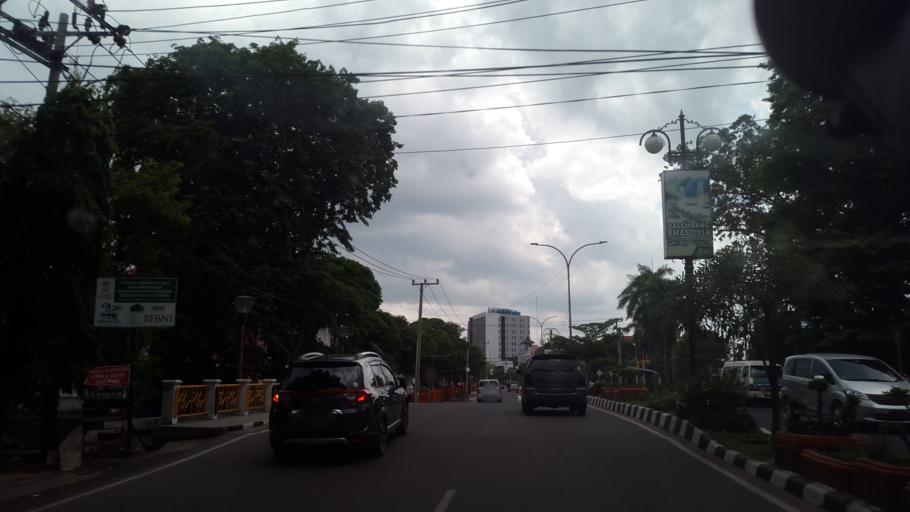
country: ID
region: South Sumatra
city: Plaju
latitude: -2.9809
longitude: 104.7457
